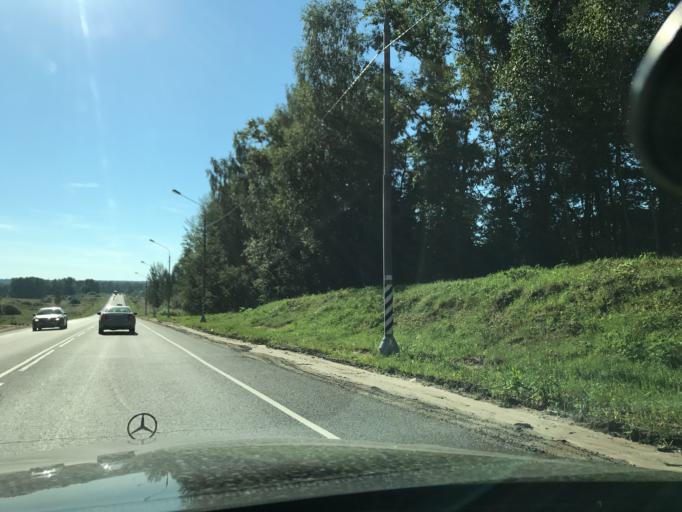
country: RU
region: Moskovskaya
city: Noginsk-9
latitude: 56.1073
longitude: 38.6266
